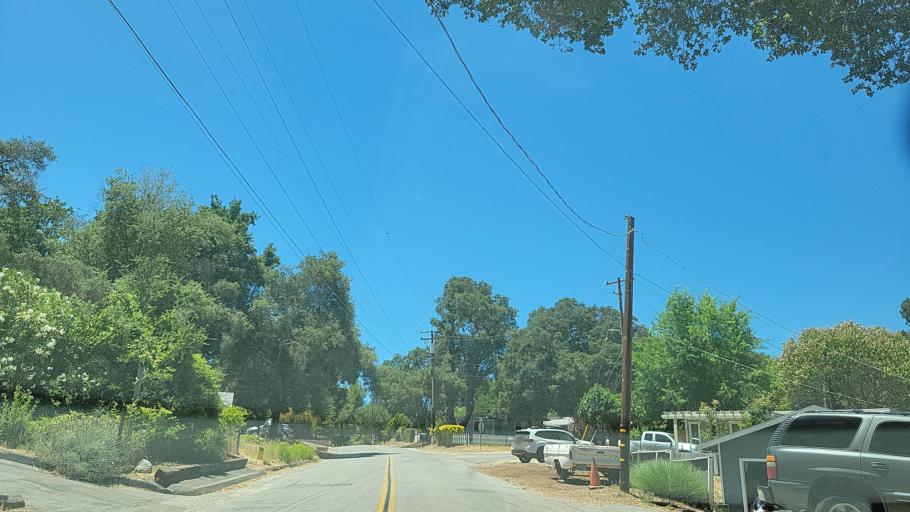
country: US
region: California
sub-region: San Luis Obispo County
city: Atascadero
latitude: 35.5081
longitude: -120.6699
